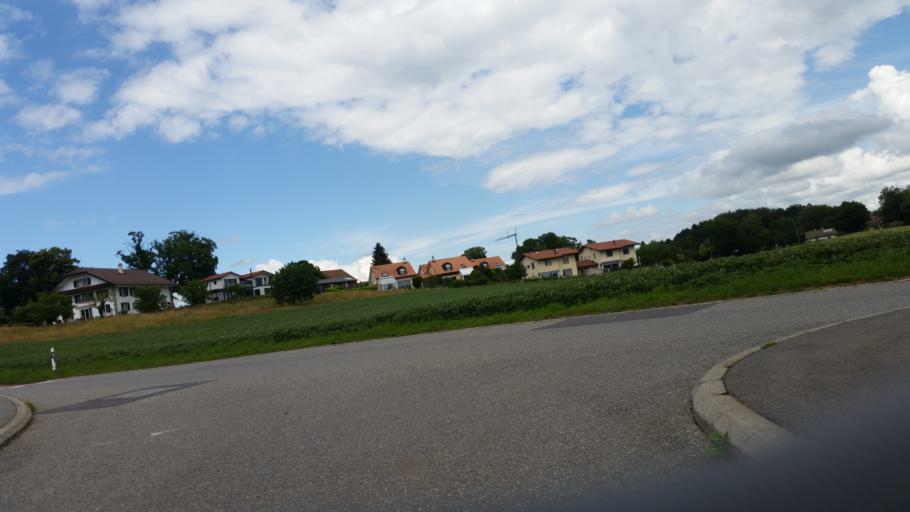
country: CH
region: Vaud
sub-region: Lausanne District
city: Cheseaux
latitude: 46.5876
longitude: 6.6279
